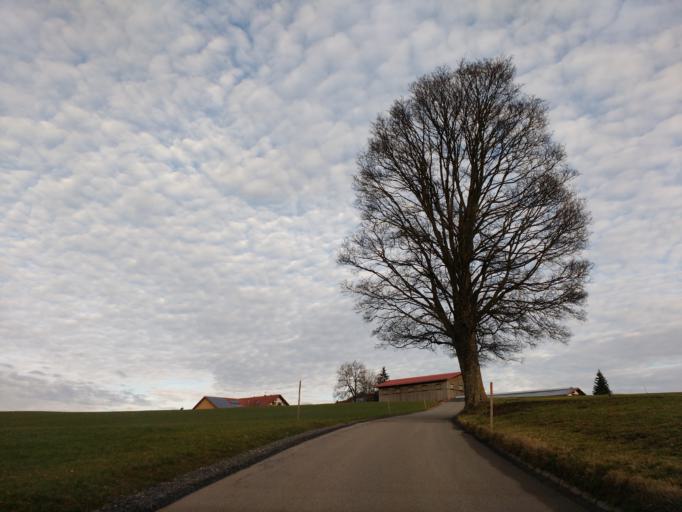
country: DE
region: Bavaria
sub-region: Swabia
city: Wildpoldsried
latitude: 47.7809
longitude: 10.4032
